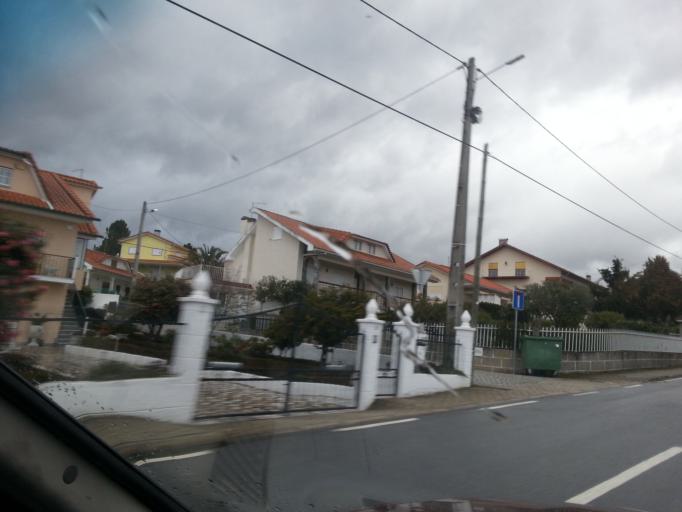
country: PT
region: Guarda
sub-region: Celorico da Beira
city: Celorico da Beira
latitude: 40.6294
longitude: -7.3423
